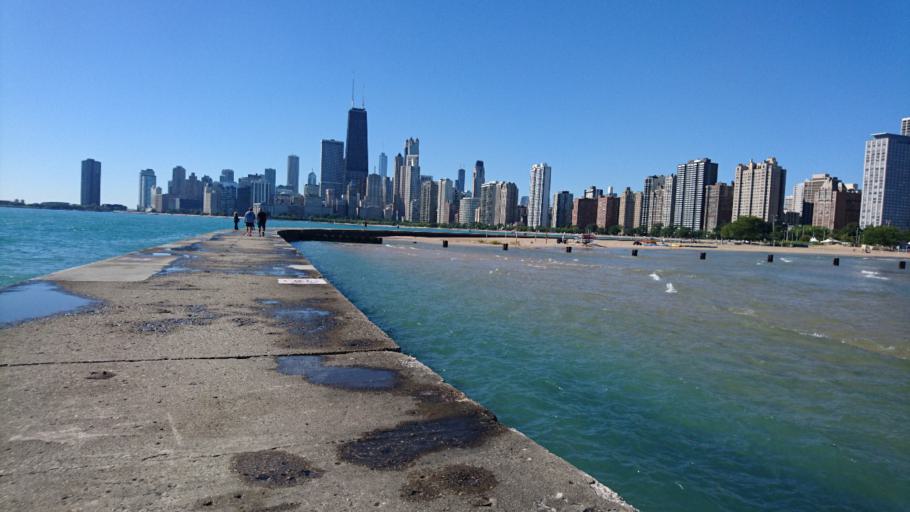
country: US
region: Illinois
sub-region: Cook County
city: Chicago
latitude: 41.9145
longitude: -87.6203
